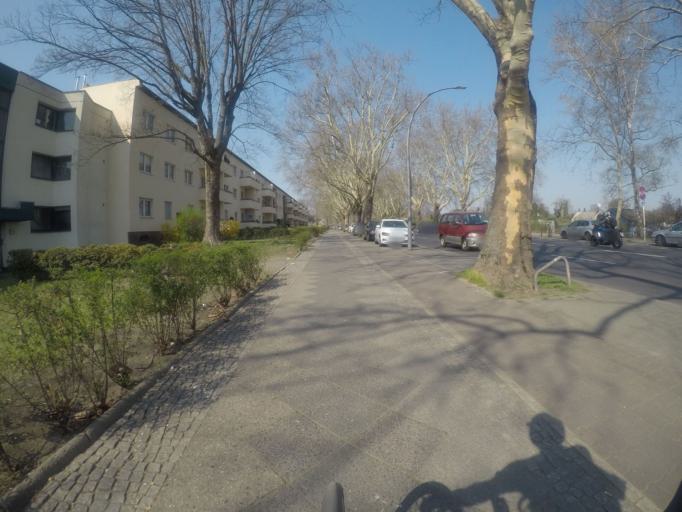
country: DE
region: Berlin
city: Reinickendorf
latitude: 52.5816
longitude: 13.3447
